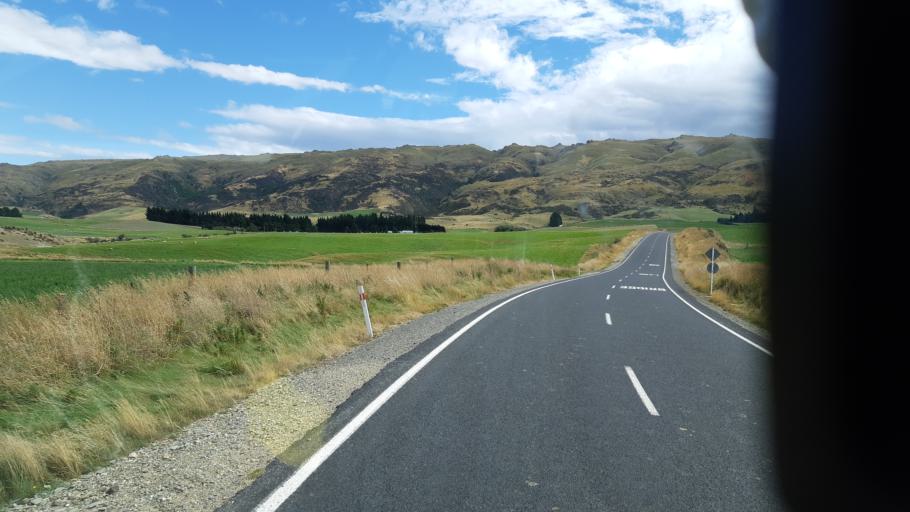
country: NZ
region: Otago
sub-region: Dunedin City
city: Dunedin
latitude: -45.3189
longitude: 170.2614
